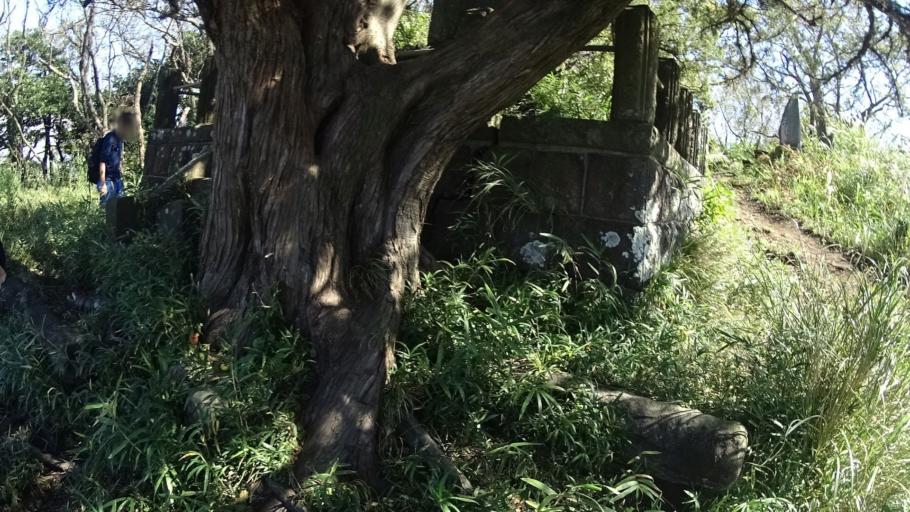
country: JP
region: Kanagawa
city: Hayama
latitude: 35.2770
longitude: 139.5825
